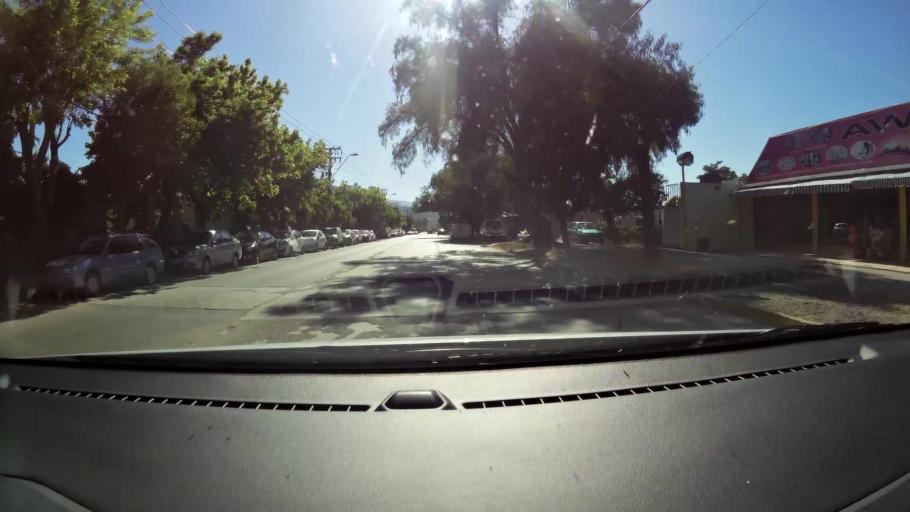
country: CL
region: Santiago Metropolitan
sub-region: Provincia de Chacabuco
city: Lampa
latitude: -33.4026
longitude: -71.1282
